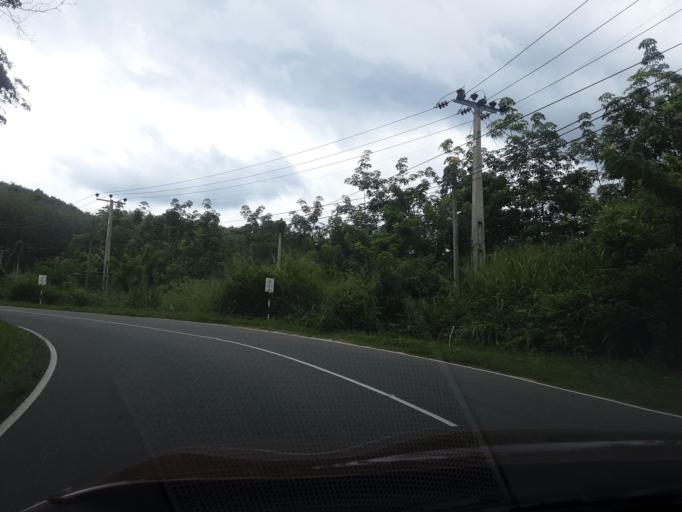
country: LK
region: Uva
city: Monaragala
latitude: 6.9020
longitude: 81.2158
